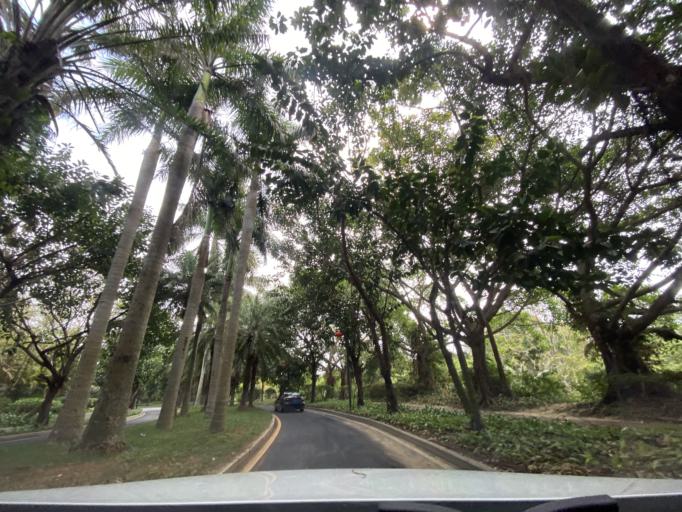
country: CN
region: Hainan
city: Liji
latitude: 18.6690
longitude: 110.2715
